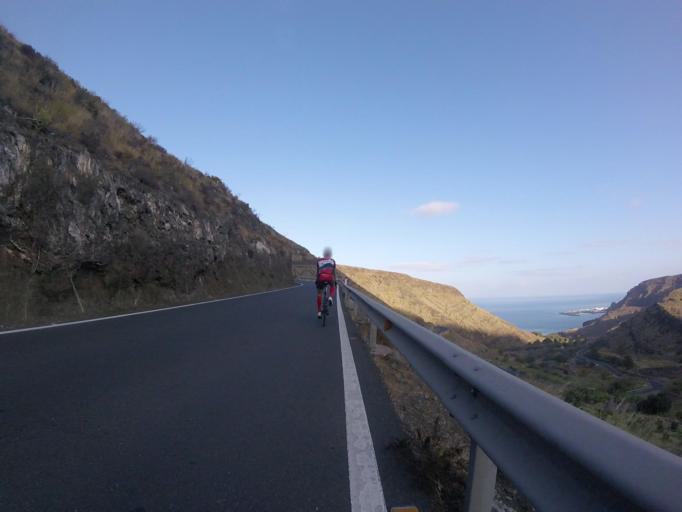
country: ES
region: Canary Islands
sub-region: Provincia de Las Palmas
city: Agaete
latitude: 28.0772
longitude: -15.7053
